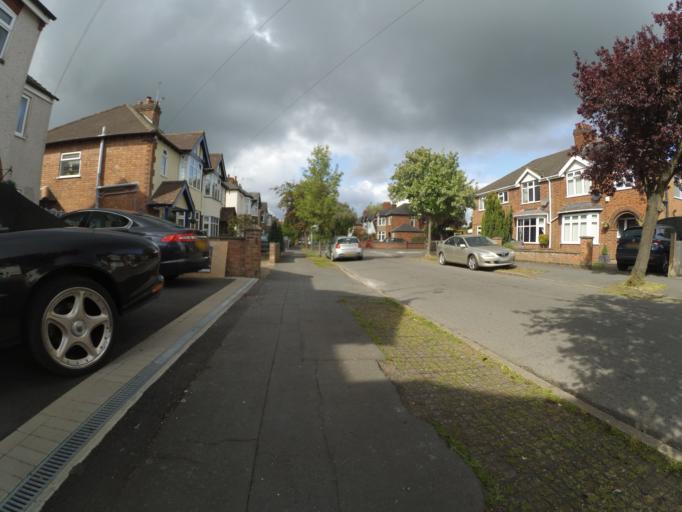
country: GB
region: England
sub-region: Warwickshire
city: Rugby
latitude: 52.3668
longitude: -1.2419
